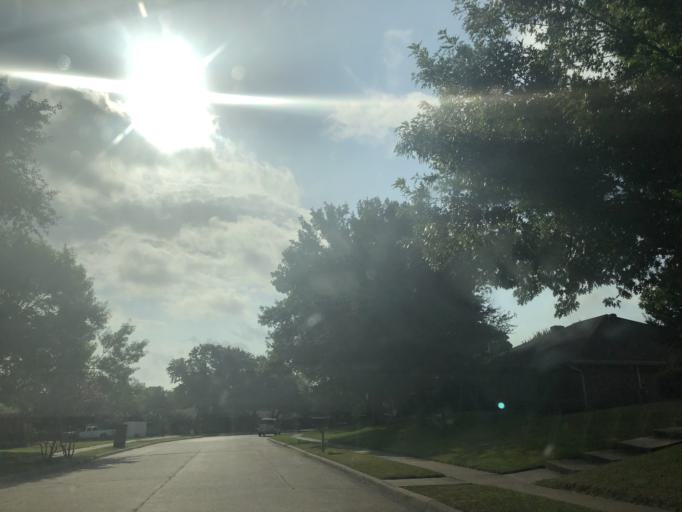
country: US
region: Texas
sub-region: Dallas County
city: Garland
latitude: 32.8581
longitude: -96.6240
